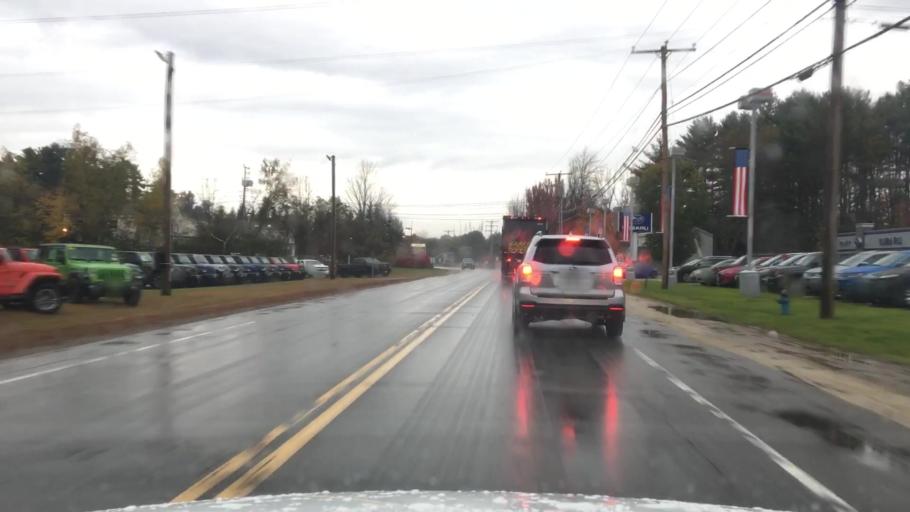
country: US
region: New Hampshire
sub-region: Strafford County
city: Somersworth
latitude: 43.2412
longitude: -70.8983
